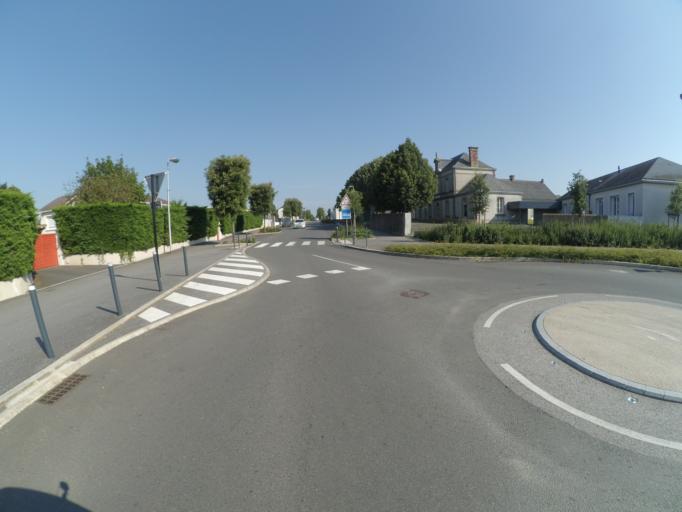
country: FR
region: Pays de la Loire
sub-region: Departement de la Vendee
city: Saint-Hilaire-de-Loulay
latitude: 47.0034
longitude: -1.3330
